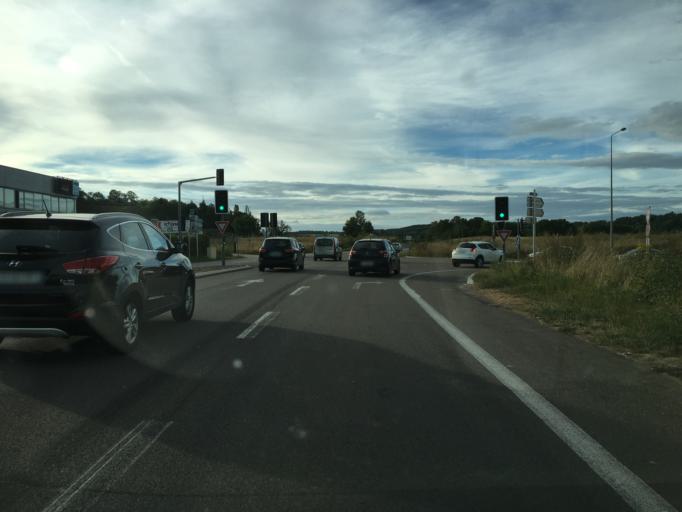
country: FR
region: Bourgogne
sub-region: Departement de la Cote-d'Or
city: Daix
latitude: 47.3447
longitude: 4.9979
